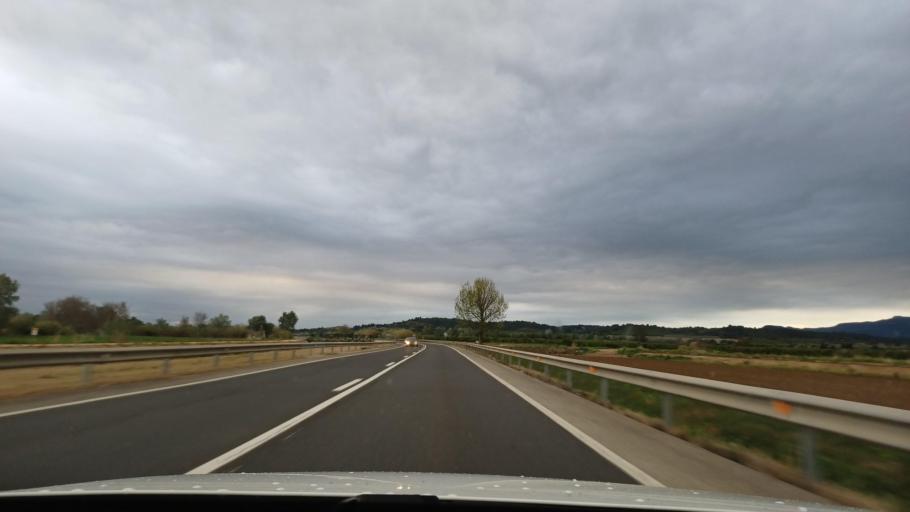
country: ES
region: Catalonia
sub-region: Provincia de Tarragona
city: Masdenverge
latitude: 40.7572
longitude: 0.5376
